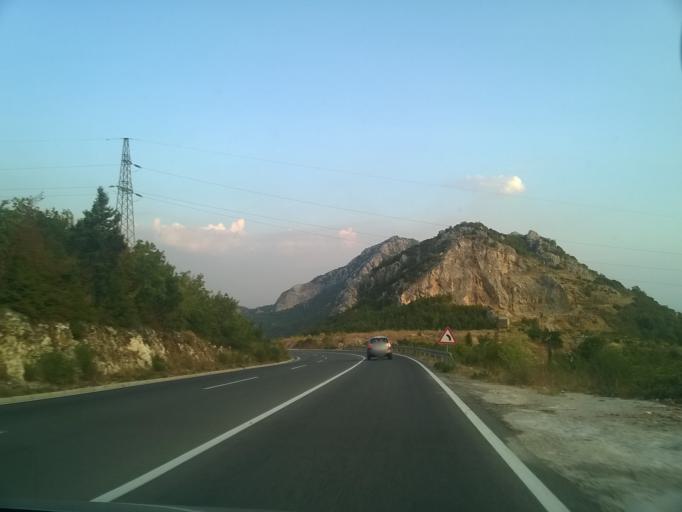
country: ME
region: Bar
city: Sutomore
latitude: 42.1733
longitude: 19.0006
